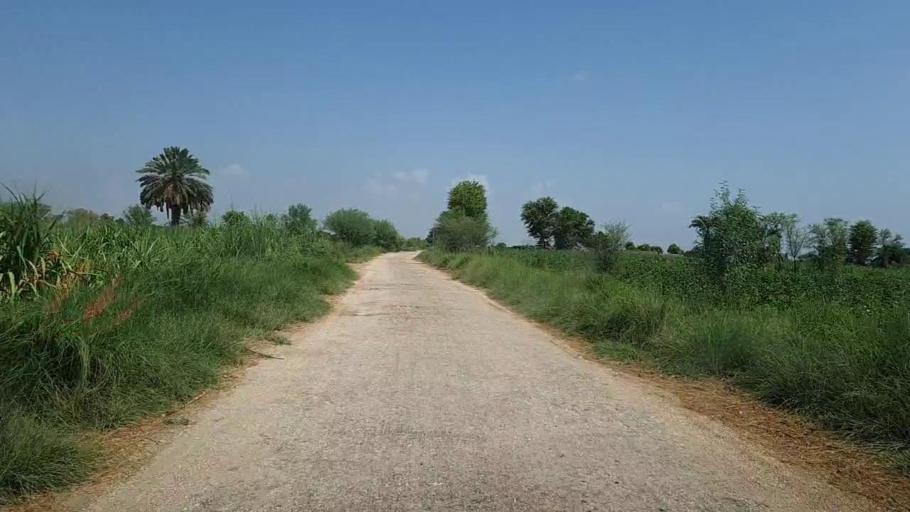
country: PK
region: Sindh
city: Bhiria
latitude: 26.8771
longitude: 68.2464
